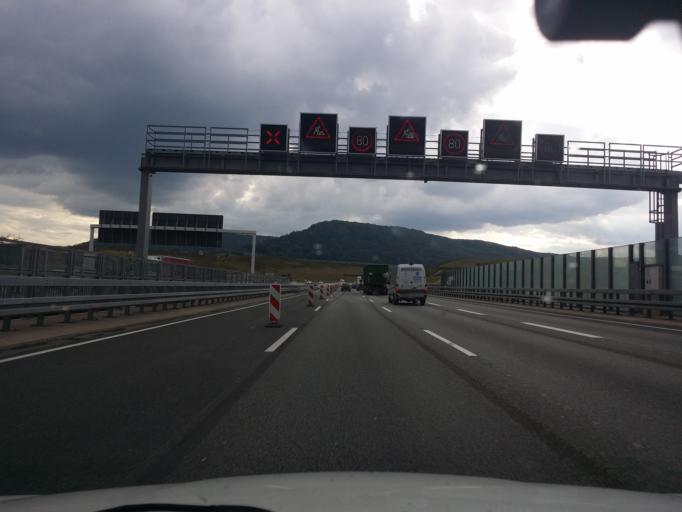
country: DE
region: Thuringia
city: Sulza
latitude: 50.8737
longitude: 11.5969
